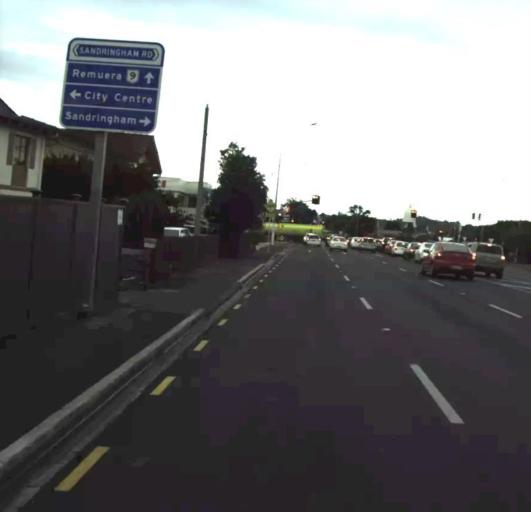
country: NZ
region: Auckland
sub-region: Auckland
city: Auckland
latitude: -36.8848
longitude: 174.7371
